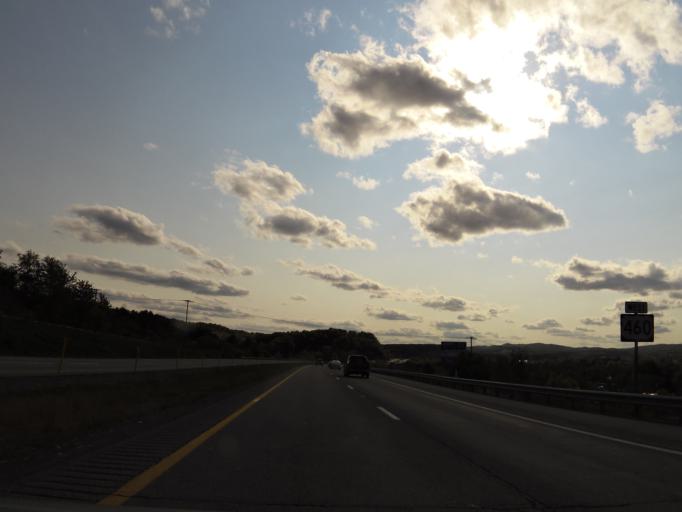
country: US
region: West Virginia
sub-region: Mercer County
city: Princeton
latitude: 37.3613
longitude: -81.0784
